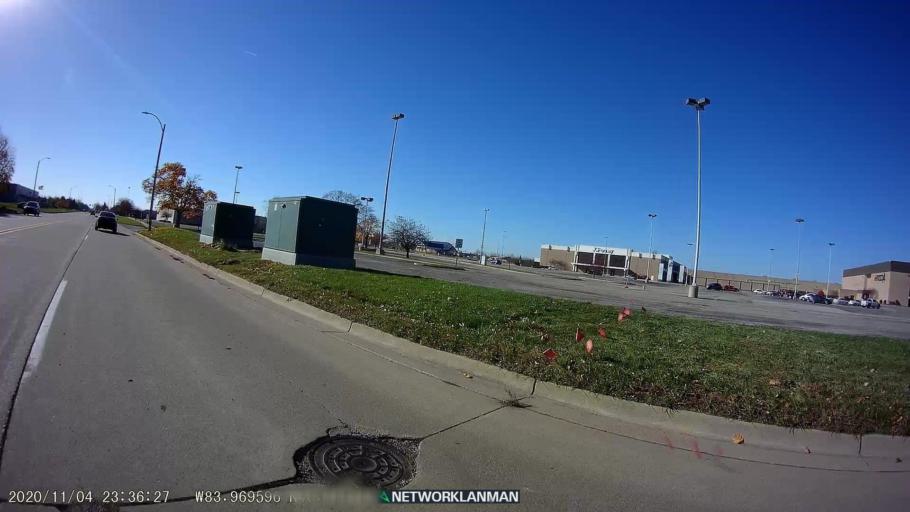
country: US
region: Michigan
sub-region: Saginaw County
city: Carrollton
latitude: 43.4753
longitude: -83.9696
